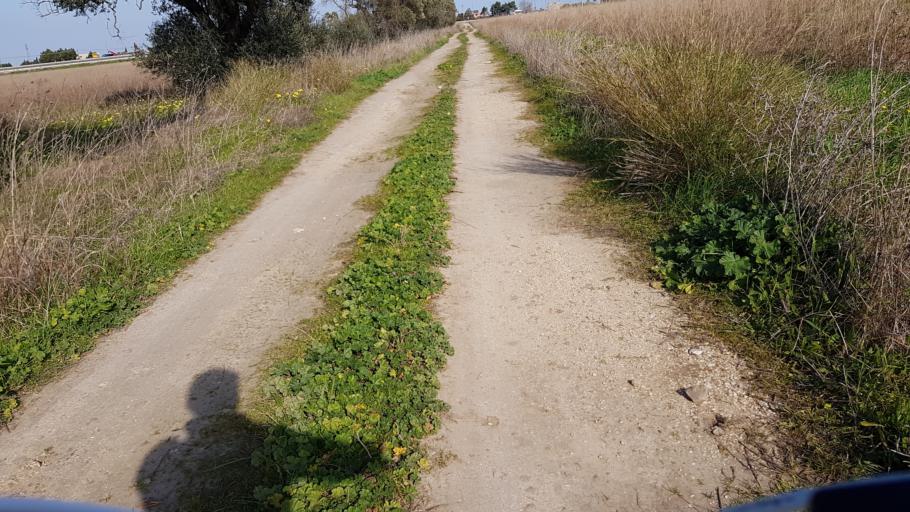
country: IT
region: Apulia
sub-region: Provincia di Brindisi
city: Brindisi
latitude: 40.6111
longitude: 17.8981
